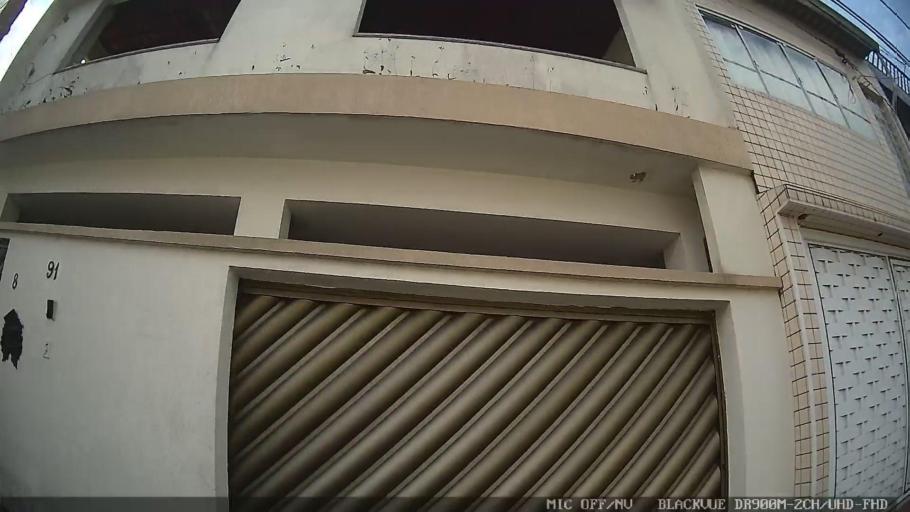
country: BR
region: Sao Paulo
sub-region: Santos
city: Santos
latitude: -23.9490
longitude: -46.2865
